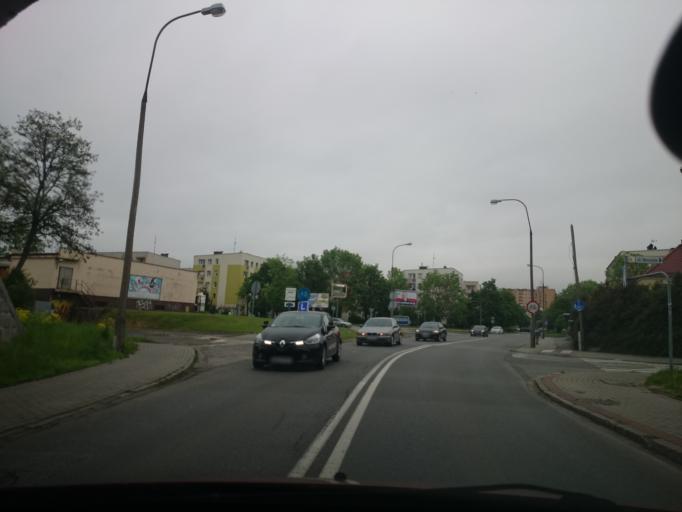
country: PL
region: Opole Voivodeship
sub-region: Powiat opolski
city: Opole
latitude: 50.6801
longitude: 17.9245
